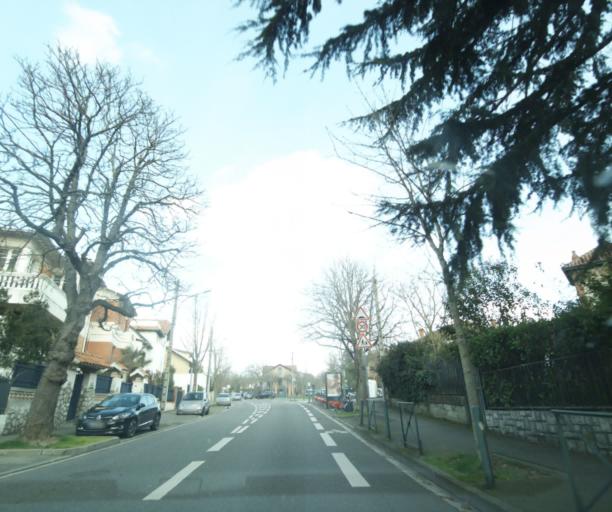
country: FR
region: Midi-Pyrenees
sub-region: Departement de la Haute-Garonne
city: Toulouse
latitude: 43.5914
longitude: 1.4697
